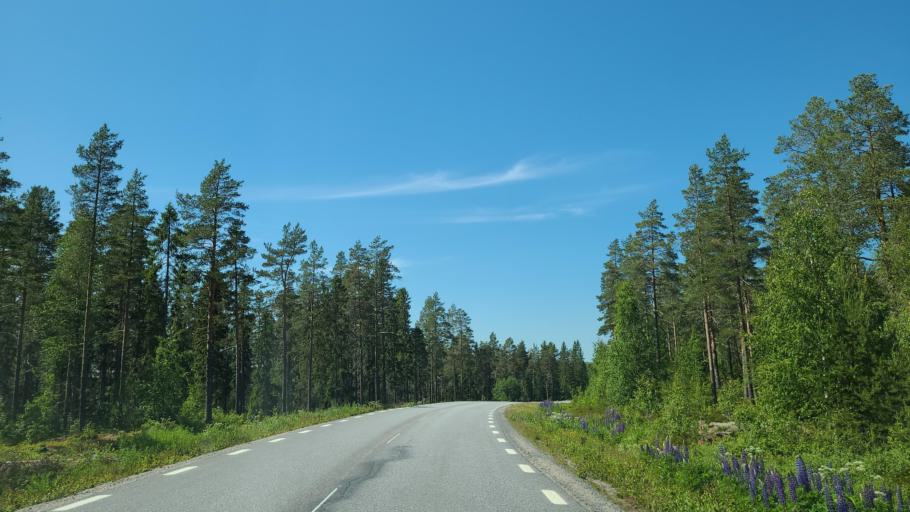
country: SE
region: Vaesternorrland
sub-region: OErnskoeldsviks Kommun
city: Husum
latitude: 63.5247
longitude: 19.1329
